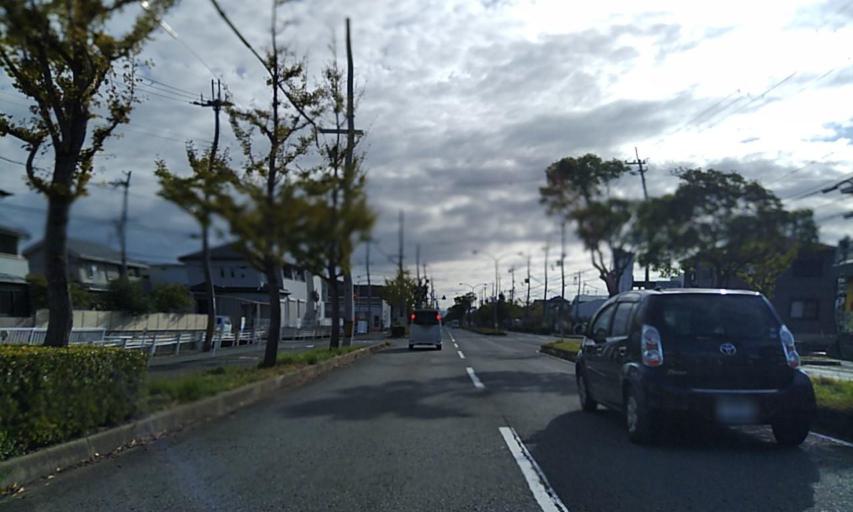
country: JP
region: Wakayama
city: Minato
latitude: 34.2562
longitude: 135.1279
